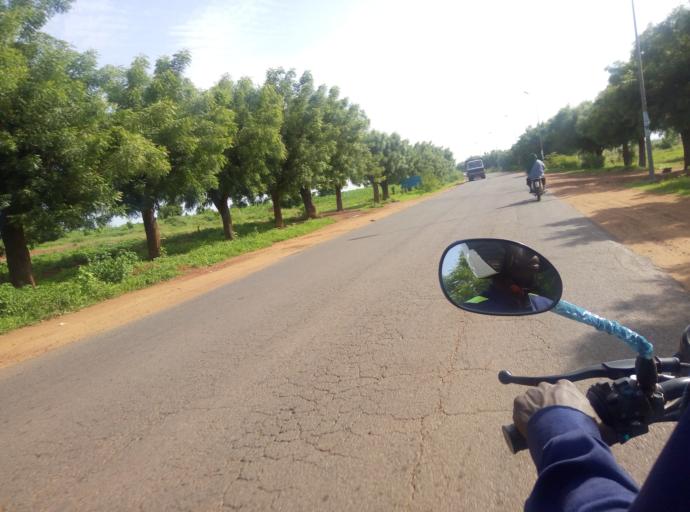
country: ML
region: Bamako
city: Bamako
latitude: 12.5546
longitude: -7.9462
